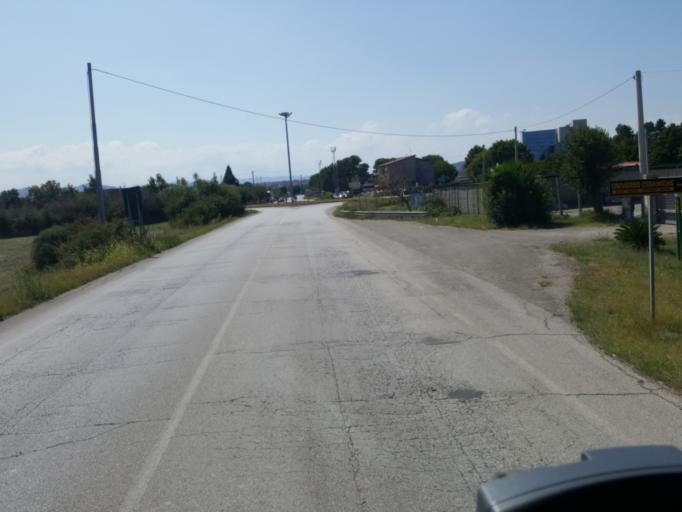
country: IT
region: Abruzzo
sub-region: Provincia di Chieti
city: Salvo Marina
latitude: 42.0578
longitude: 14.7584
